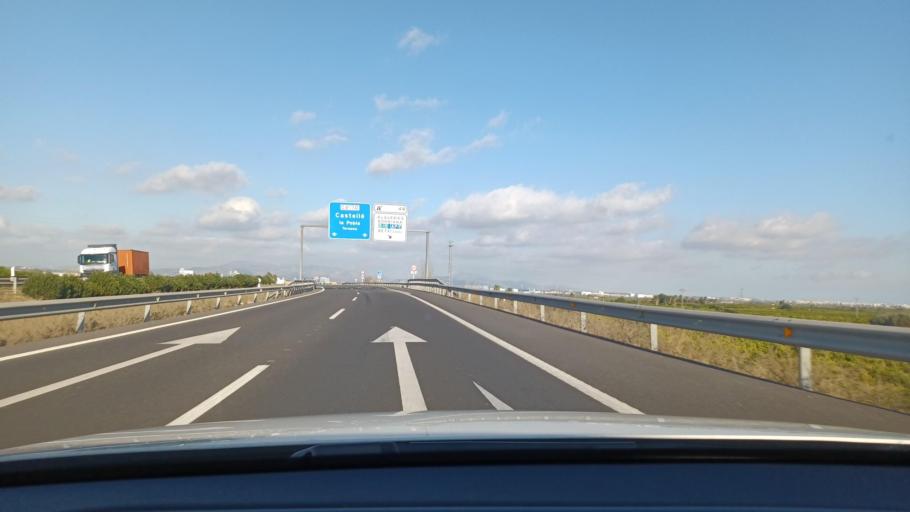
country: ES
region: Valencia
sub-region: Provincia de Castello
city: Betxi
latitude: 39.9232
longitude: -0.1931
